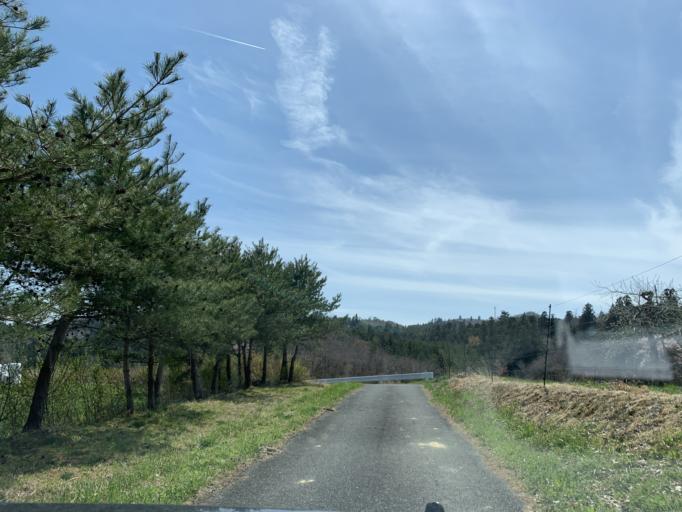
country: JP
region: Iwate
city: Ichinoseki
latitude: 38.8397
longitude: 141.2887
